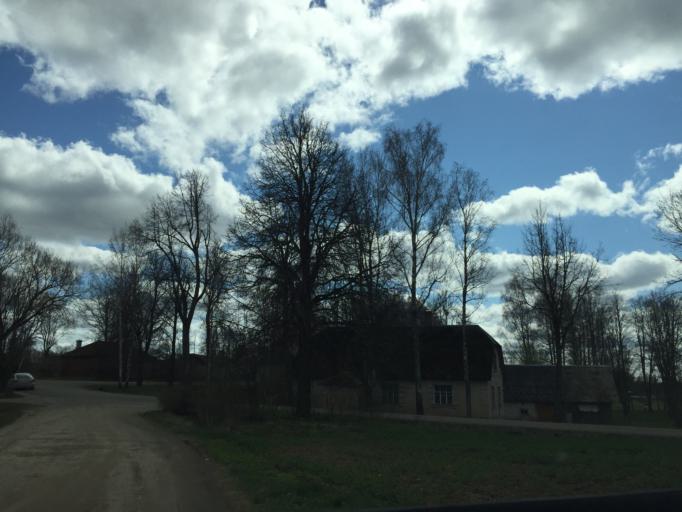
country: LV
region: Rezekne
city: Rezekne
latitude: 56.6517
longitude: 27.1873
